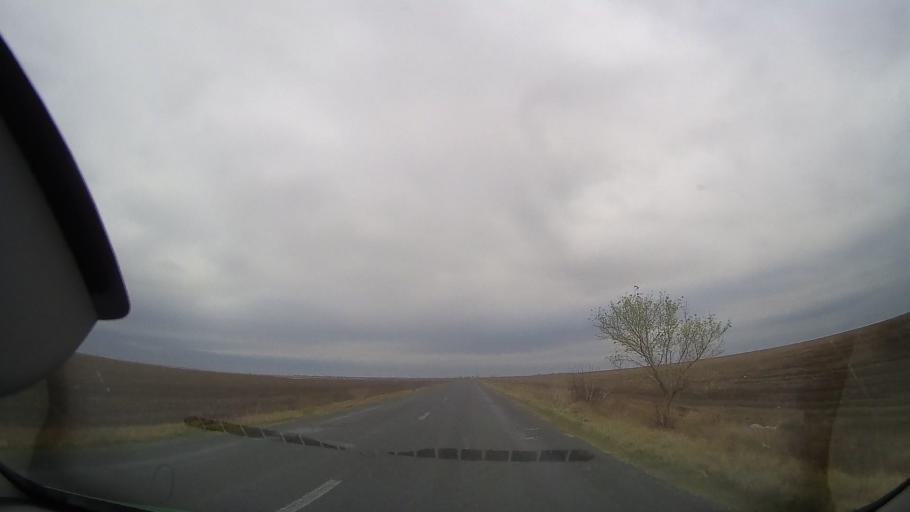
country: RO
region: Buzau
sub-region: Comuna Padina
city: Padina
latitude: 44.8093
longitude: 27.1281
